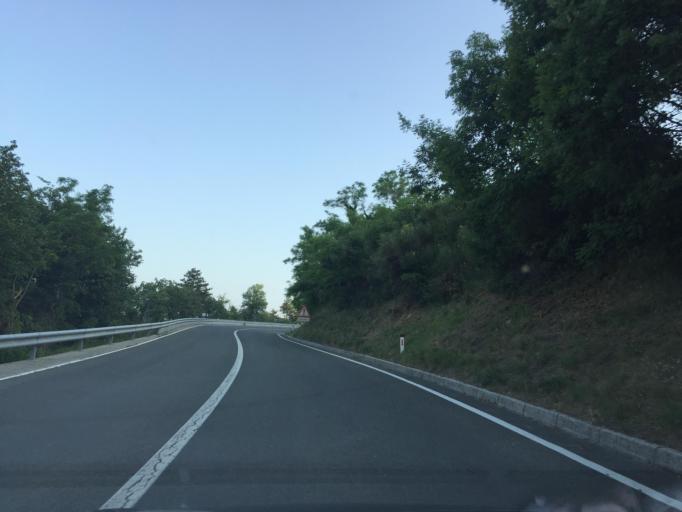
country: IT
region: Friuli Venezia Giulia
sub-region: Provincia di Trieste
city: Dolina
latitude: 45.5531
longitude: 13.8768
